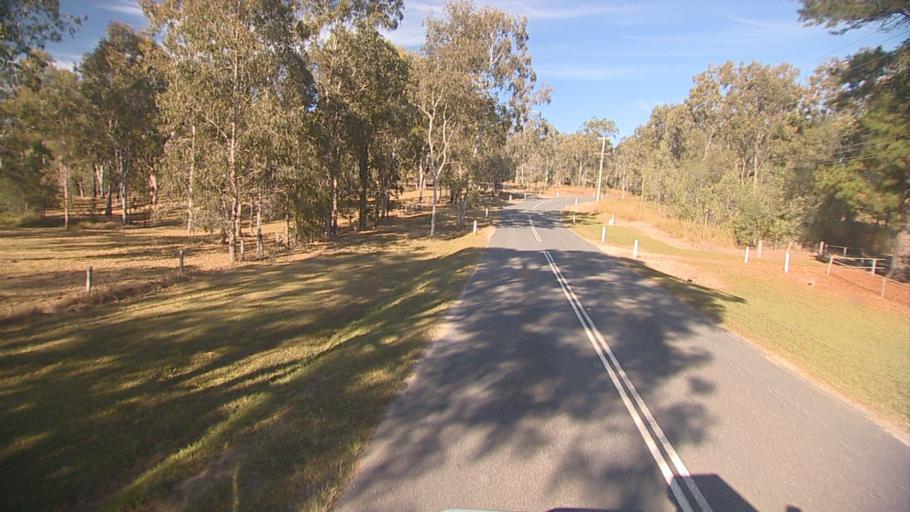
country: AU
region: Queensland
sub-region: Logan
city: Windaroo
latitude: -27.8114
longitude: 153.1705
